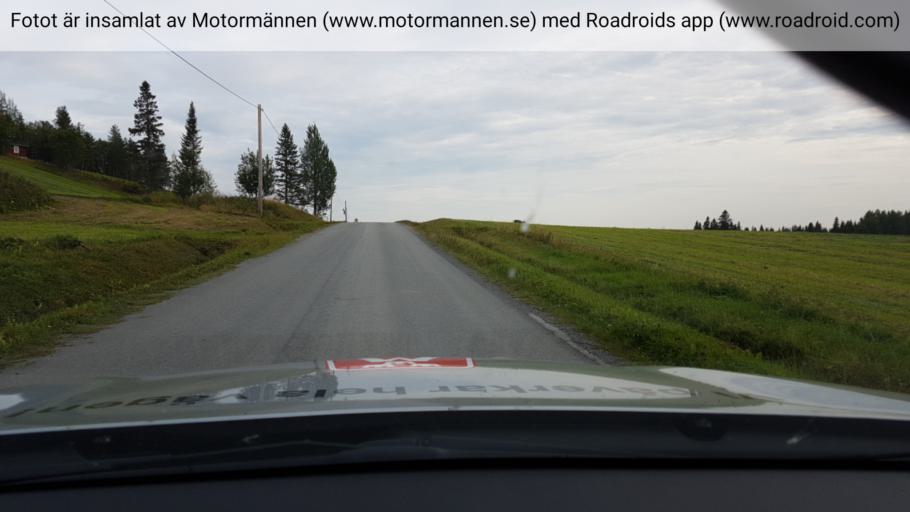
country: SE
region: Jaemtland
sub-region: OEstersunds Kommun
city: Lit
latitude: 63.6432
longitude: 14.9554
